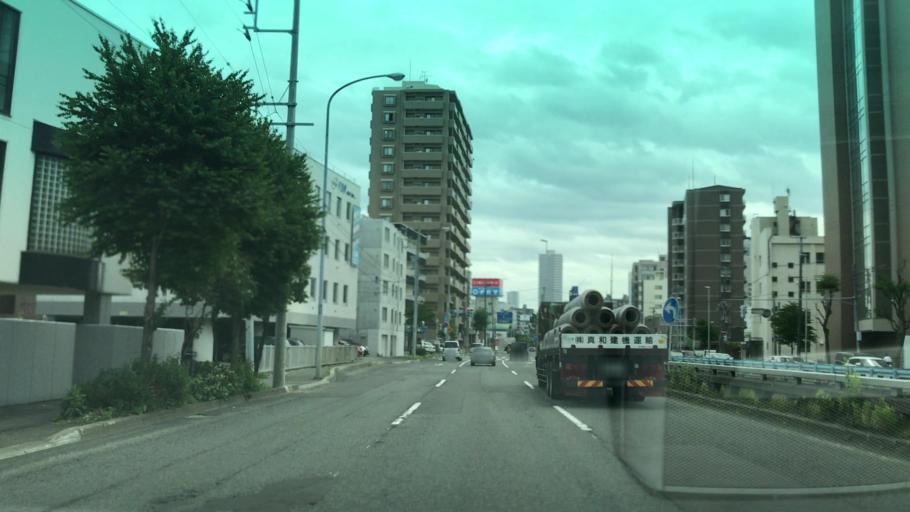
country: JP
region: Hokkaido
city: Sapporo
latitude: 43.0808
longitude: 141.3513
